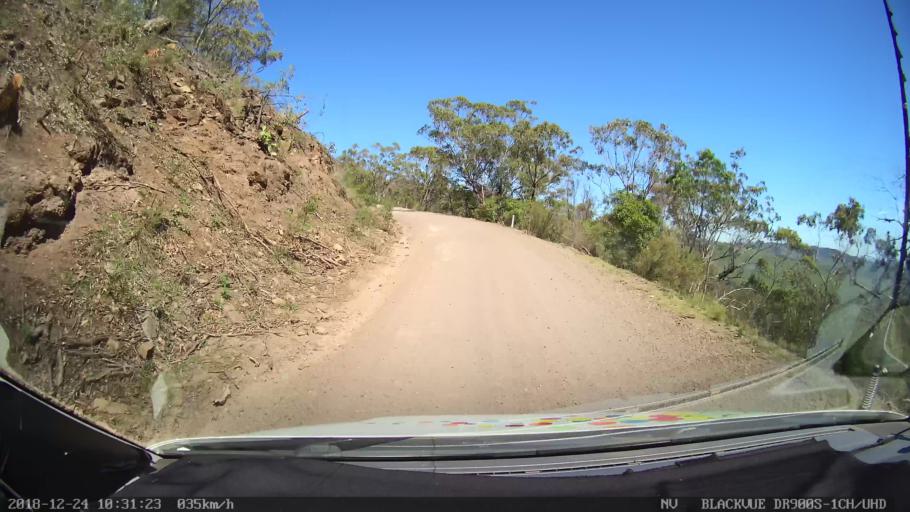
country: AU
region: New South Wales
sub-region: Upper Hunter Shire
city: Merriwa
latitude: -31.8393
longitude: 150.5224
